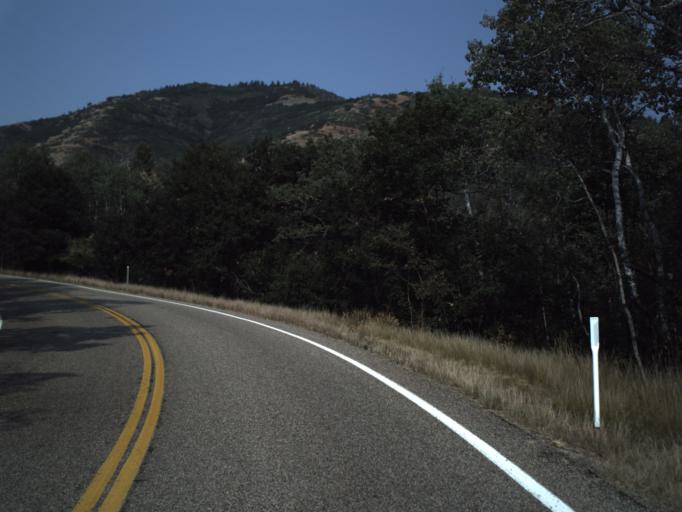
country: US
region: Utah
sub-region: Summit County
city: Summit Park
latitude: 40.8494
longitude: -111.6274
